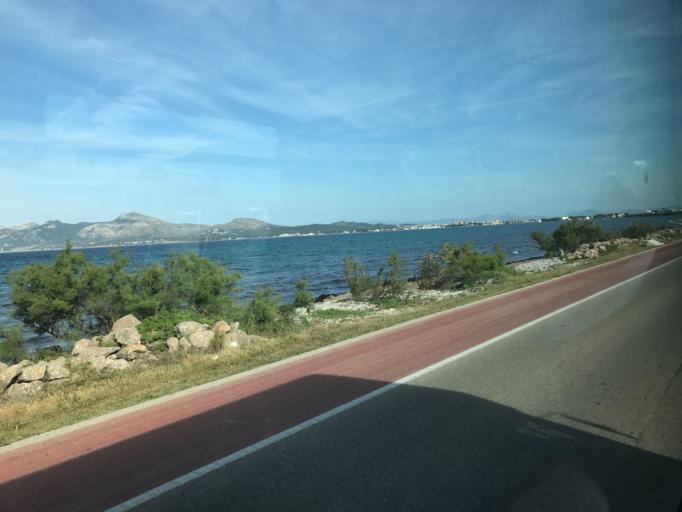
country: ES
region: Balearic Islands
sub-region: Illes Balears
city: Alcudia
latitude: 39.8763
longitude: 3.0830
